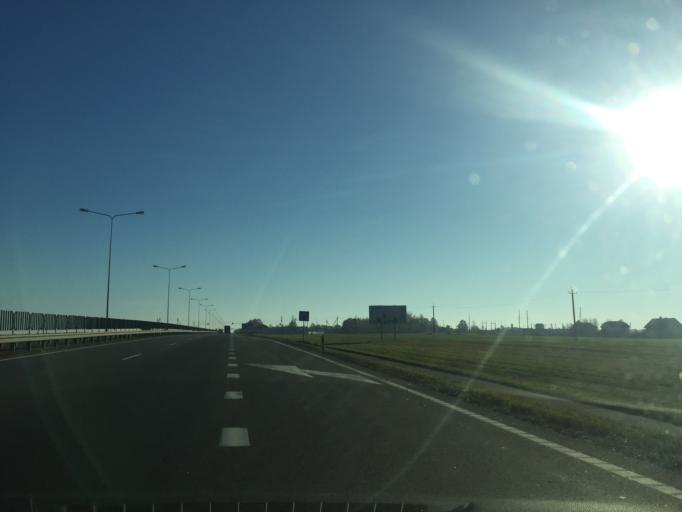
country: BY
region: Minsk
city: Smilavichy
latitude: 53.7595
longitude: 27.9966
